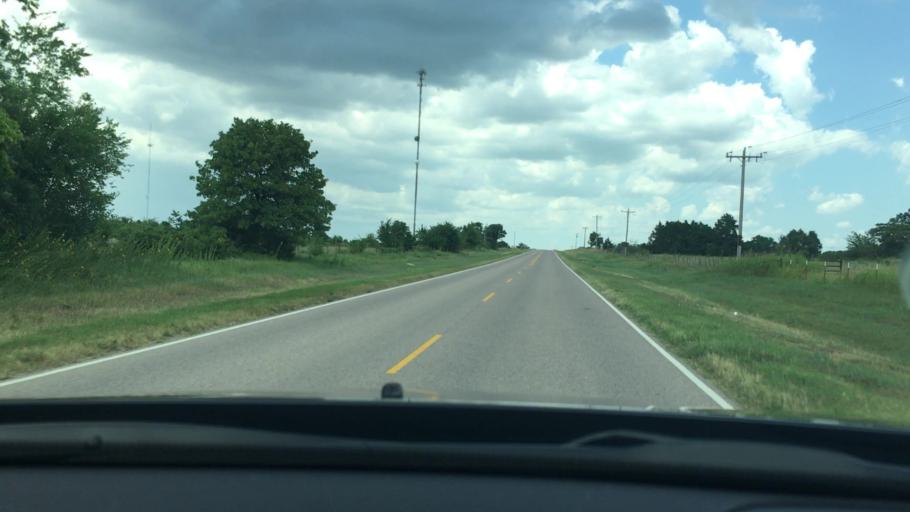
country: US
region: Oklahoma
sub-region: Johnston County
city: Tishomingo
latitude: 34.4279
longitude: -96.6360
